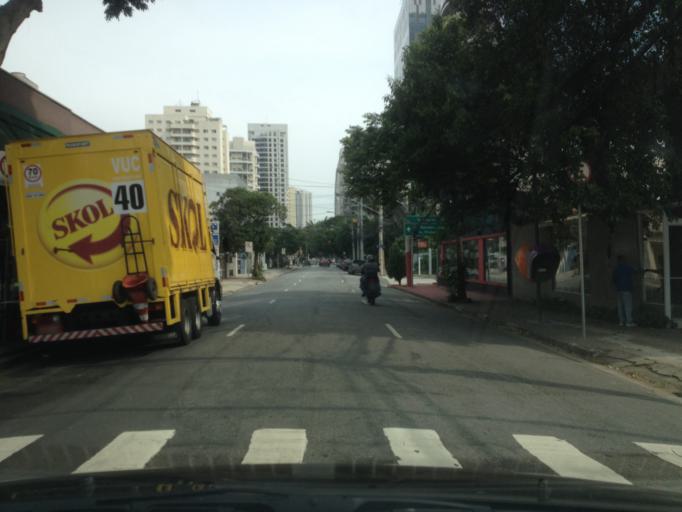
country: BR
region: Sao Paulo
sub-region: Sao Paulo
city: Sao Paulo
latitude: -23.5921
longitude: -46.6799
